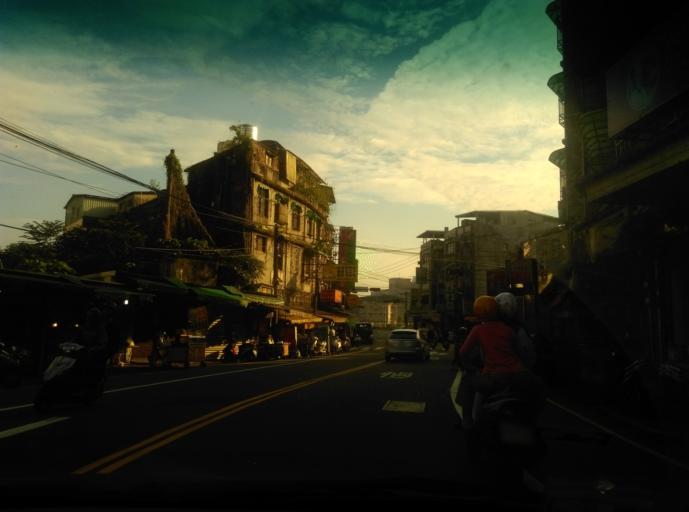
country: TW
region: Taiwan
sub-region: Keelung
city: Keelung
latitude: 25.1461
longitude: 121.7387
